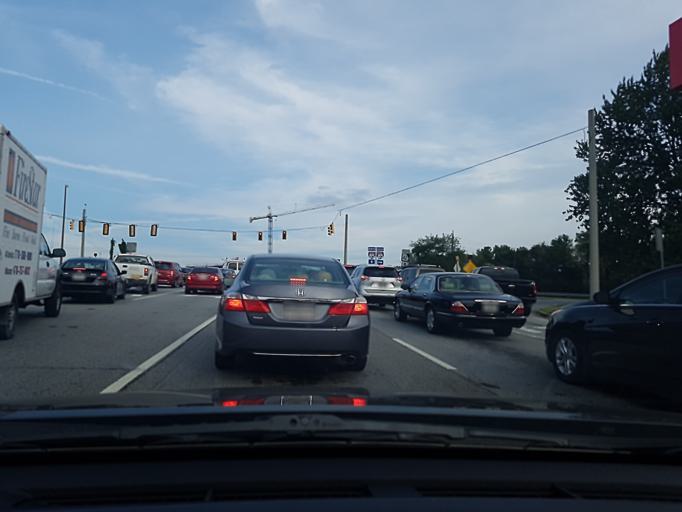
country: US
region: Georgia
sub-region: DeKalb County
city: North Druid Hills
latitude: 33.8326
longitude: -84.3370
